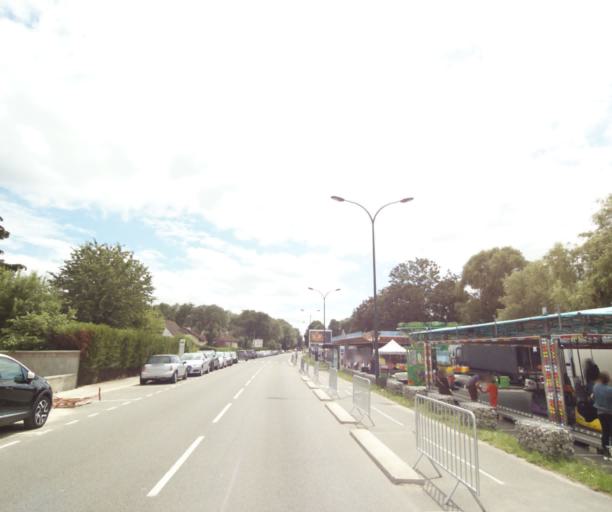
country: FR
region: Ile-de-France
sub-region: Departement des Yvelines
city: Saint-Cyr-l'Ecole
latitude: 48.7943
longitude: 2.0638
